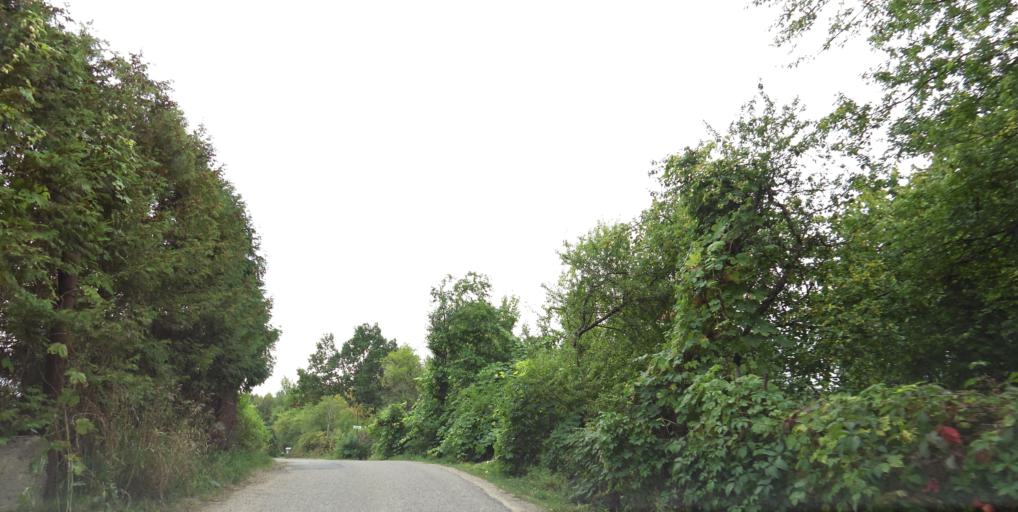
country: LT
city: Grigiskes
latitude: 54.7568
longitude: 25.0283
